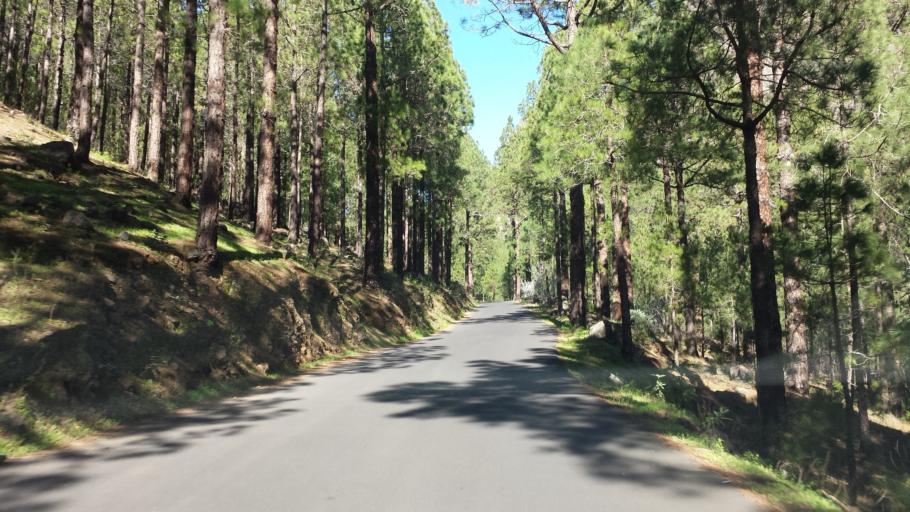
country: ES
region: Canary Islands
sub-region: Provincia de Santa Cruz de Tenerife
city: El Paso
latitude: 28.6883
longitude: -17.8500
